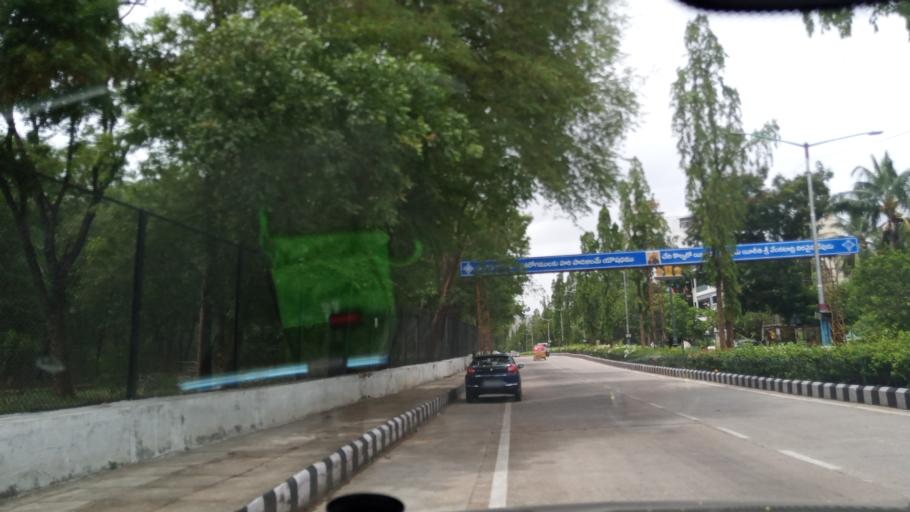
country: IN
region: Andhra Pradesh
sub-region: Chittoor
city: Akkarampalle
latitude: 13.6503
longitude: 79.4137
